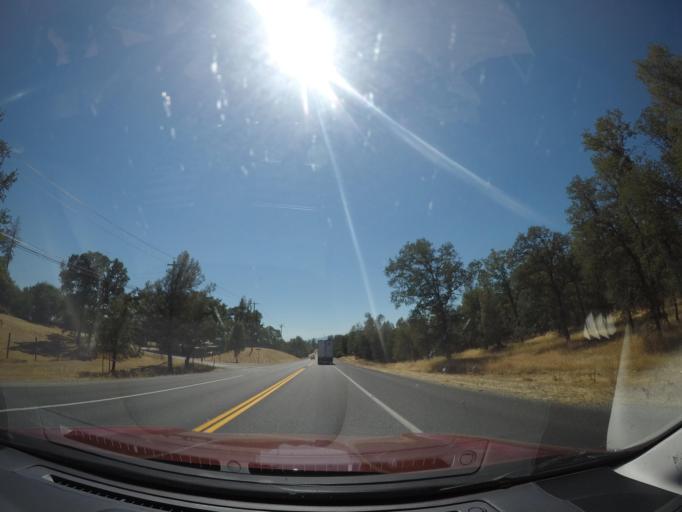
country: US
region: California
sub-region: Shasta County
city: Bella Vista
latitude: 40.6305
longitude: -122.2738
